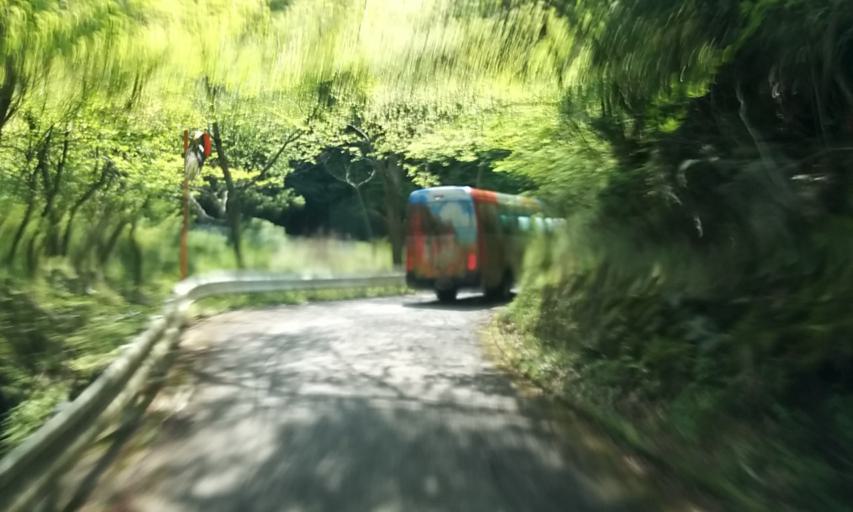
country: JP
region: Ehime
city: Niihama
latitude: 33.8741
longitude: 133.3056
